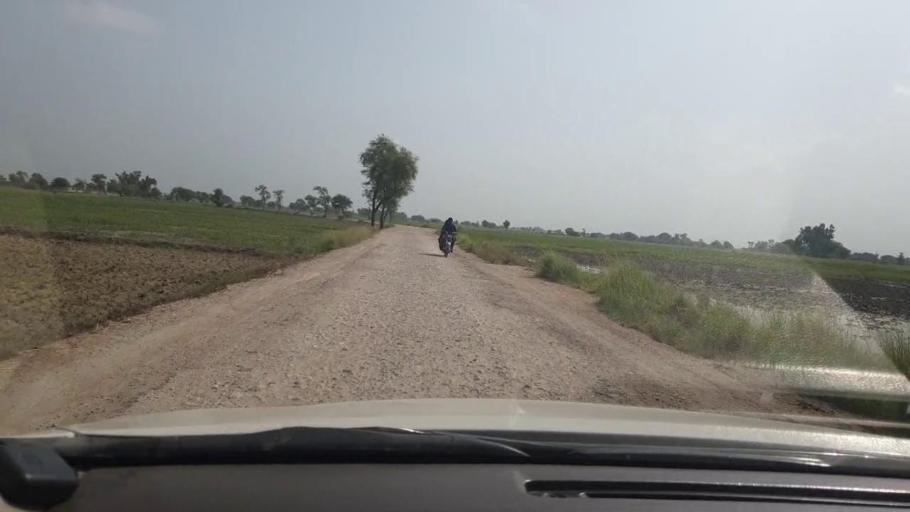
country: PK
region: Sindh
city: Shikarpur
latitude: 27.9962
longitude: 68.5940
